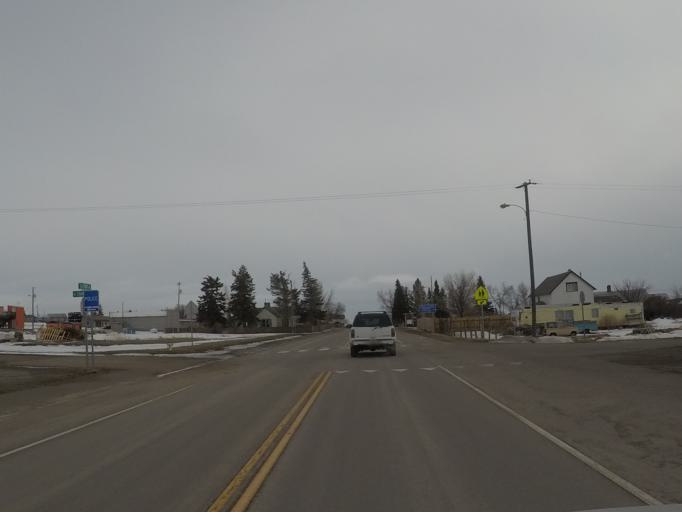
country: US
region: Montana
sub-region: Meagher County
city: White Sulphur Springs
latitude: 46.5453
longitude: -110.9064
